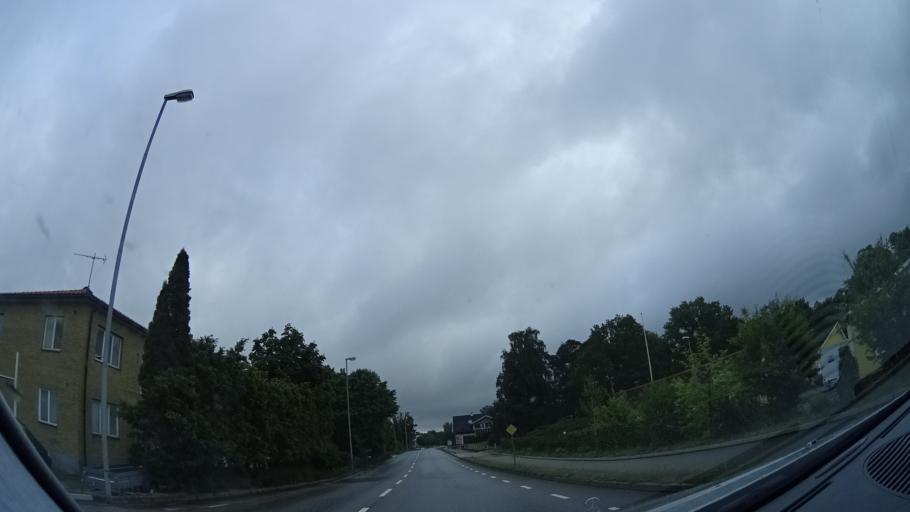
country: SE
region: Skane
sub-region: Hoors Kommun
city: Satofta
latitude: 55.9232
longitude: 13.5424
